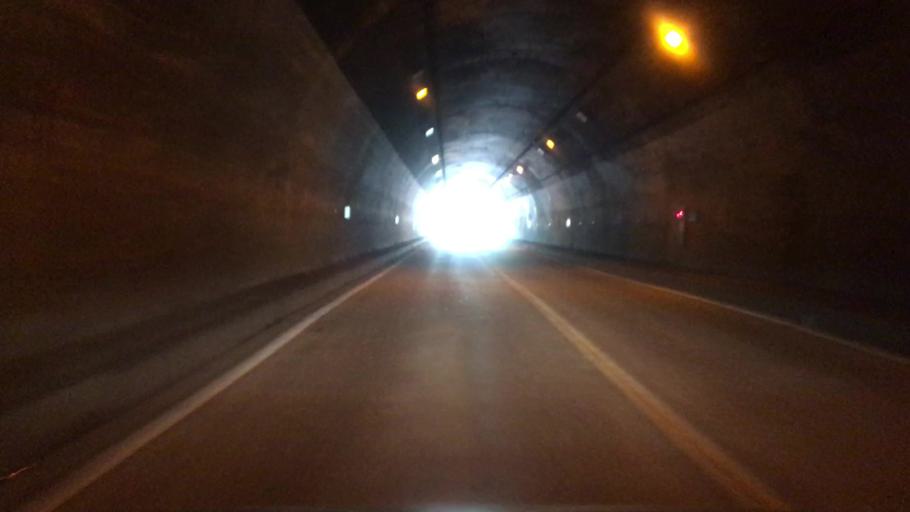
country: JP
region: Hyogo
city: Toyooka
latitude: 35.5831
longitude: 134.7424
